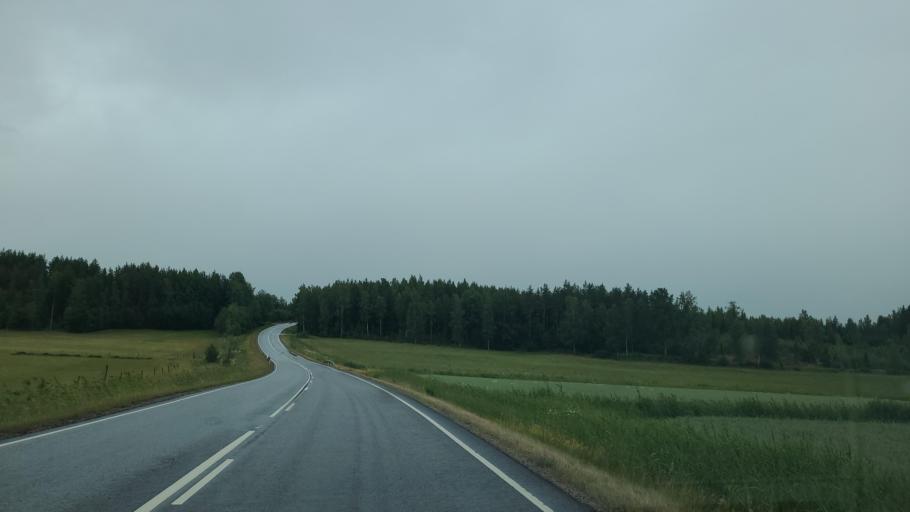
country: FI
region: Varsinais-Suomi
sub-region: Turku
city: Sauvo
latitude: 60.2902
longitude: 22.6725
